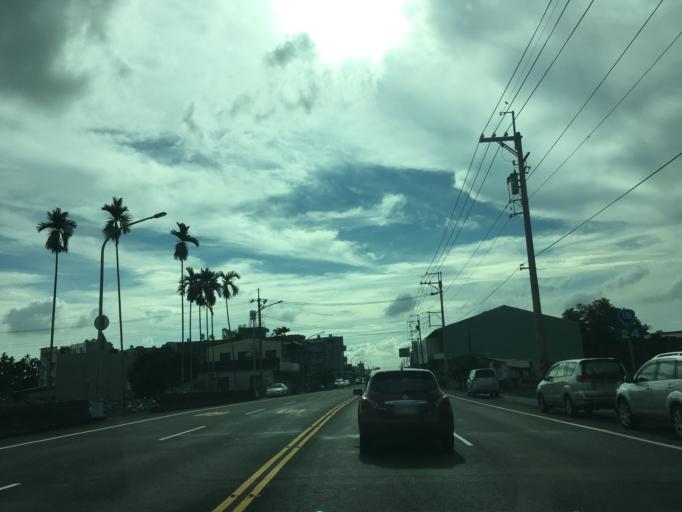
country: TW
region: Taiwan
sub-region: Chiayi
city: Jiayi Shi
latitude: 23.4424
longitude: 120.5147
